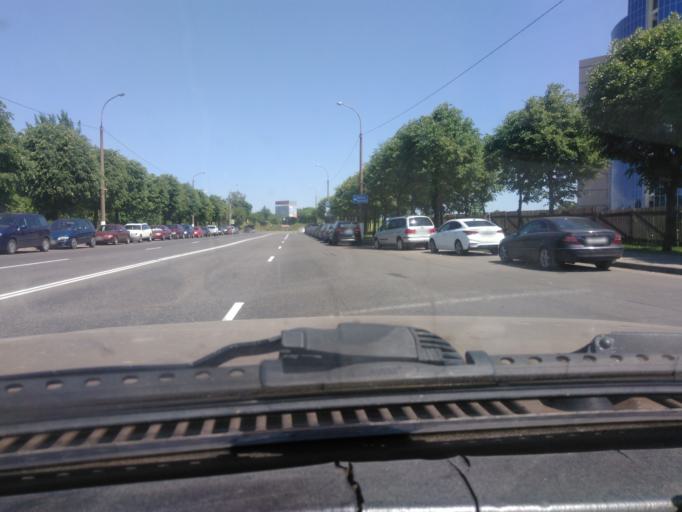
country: BY
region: Mogilev
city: Mahilyow
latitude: 53.9171
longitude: 30.3741
